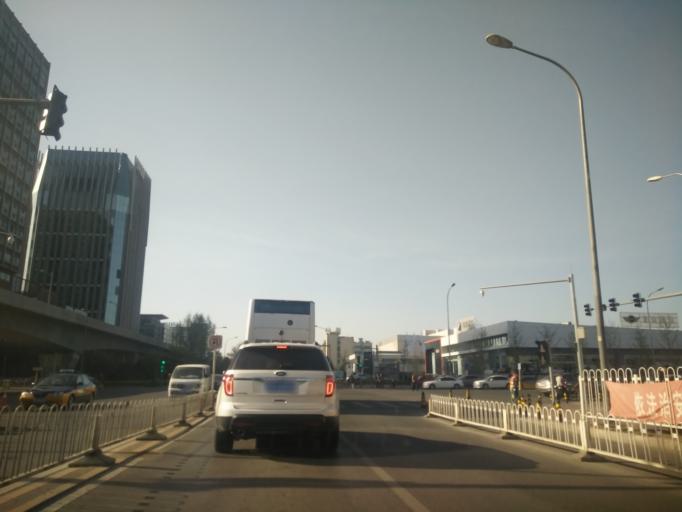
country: CN
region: Beijing
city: Jiugong
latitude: 39.7934
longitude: 116.5067
